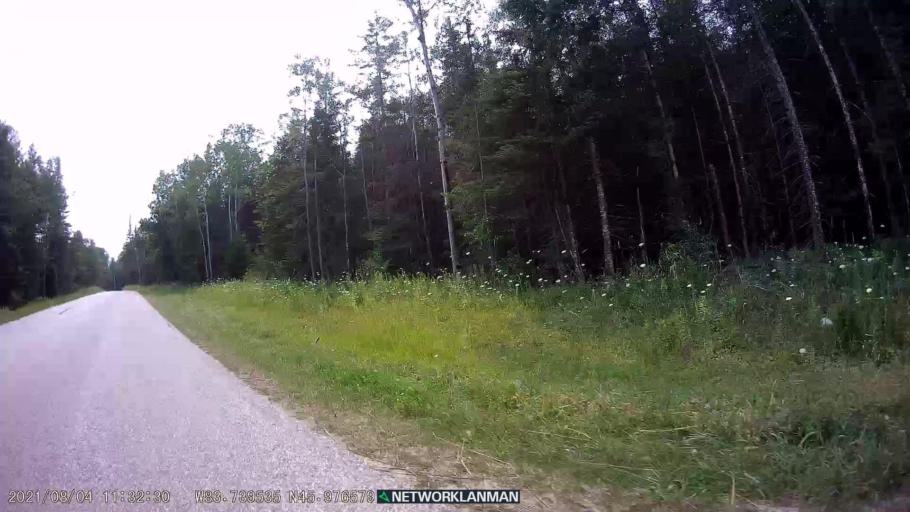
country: CA
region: Ontario
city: Thessalon
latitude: 45.9762
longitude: -83.7397
